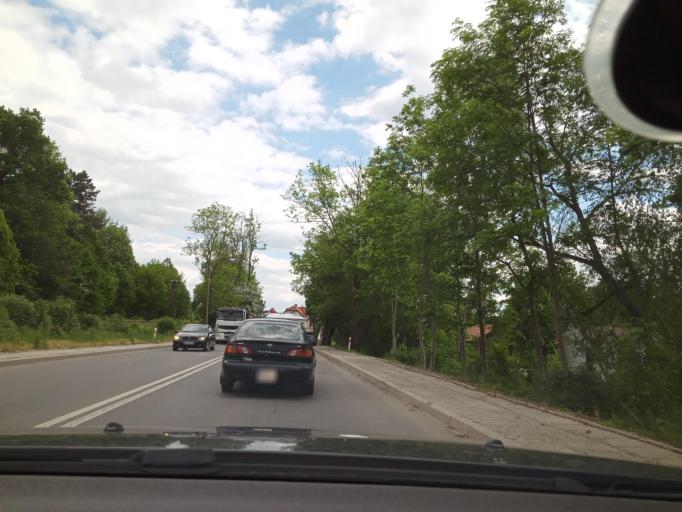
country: PL
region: Lesser Poland Voivodeship
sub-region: Powiat limanowski
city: Limanowa
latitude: 49.7254
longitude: 20.4017
